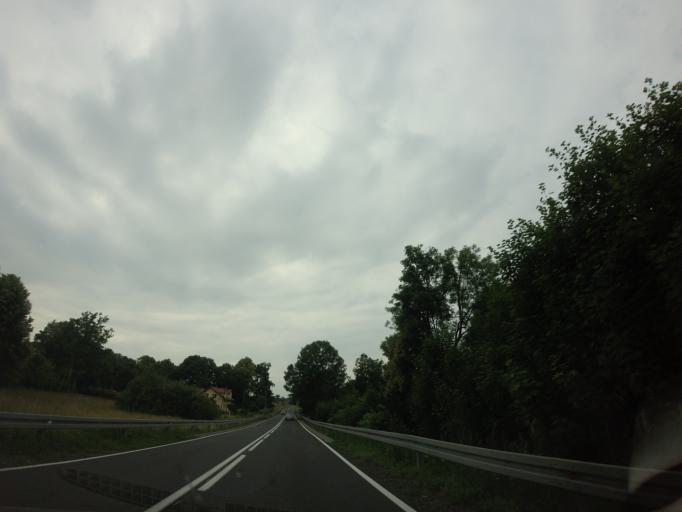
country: PL
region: West Pomeranian Voivodeship
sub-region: Powiat szczecinecki
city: Borne Sulinowo
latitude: 53.6265
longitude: 16.5101
